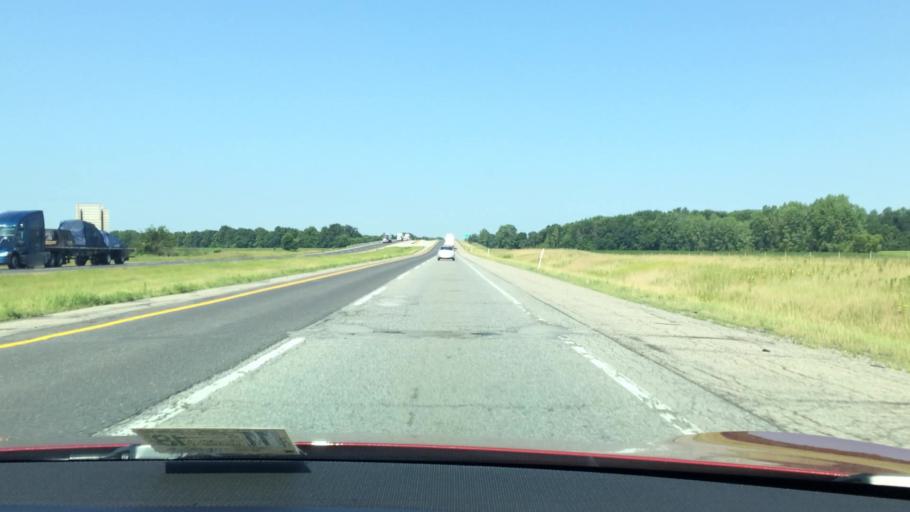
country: US
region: Michigan
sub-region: Saint Joseph County
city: Sturgis
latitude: 41.7538
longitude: -85.4411
